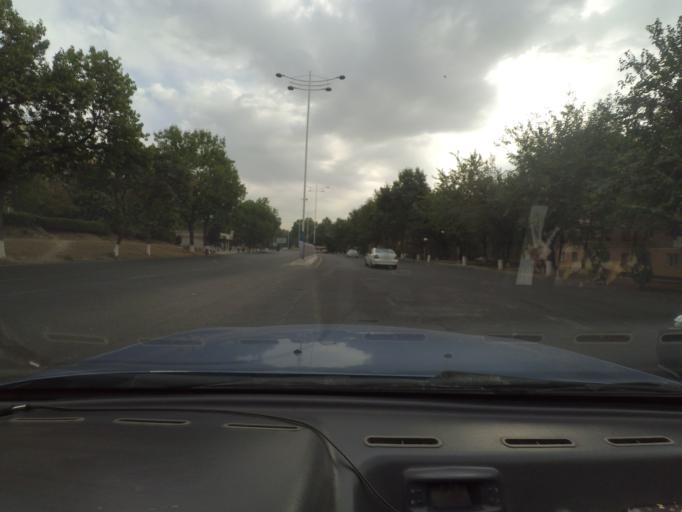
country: UZ
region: Toshkent
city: Salor
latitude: 41.3592
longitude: 69.3881
